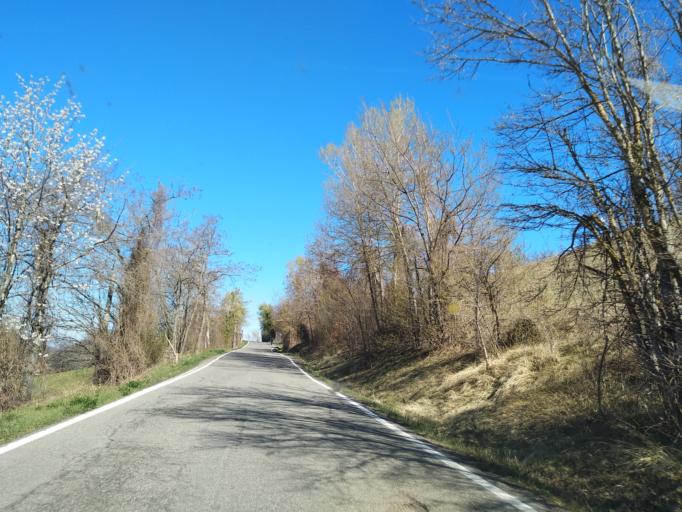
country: IT
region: Emilia-Romagna
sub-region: Provincia di Reggio Emilia
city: Castelnovo ne'Monti
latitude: 44.4186
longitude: 10.4035
